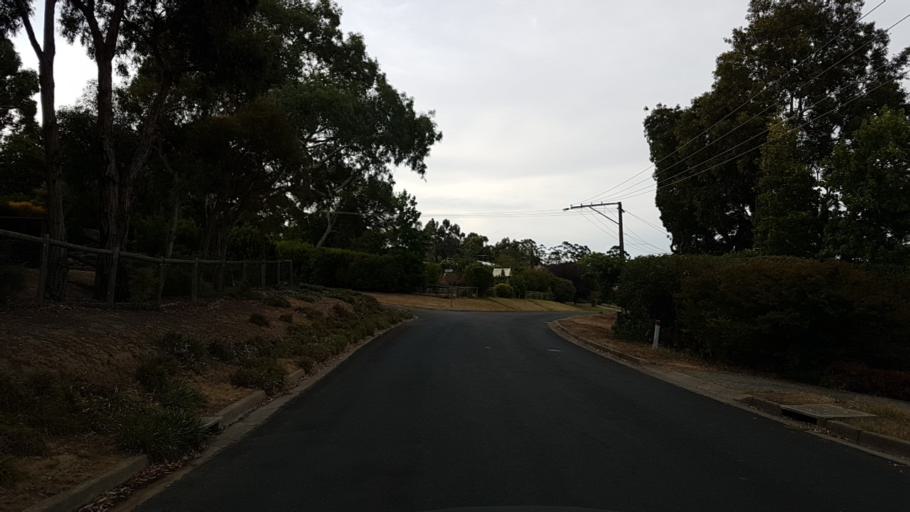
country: AU
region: South Australia
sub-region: Mount Barker
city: Nairne
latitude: -35.0306
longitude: 138.9099
